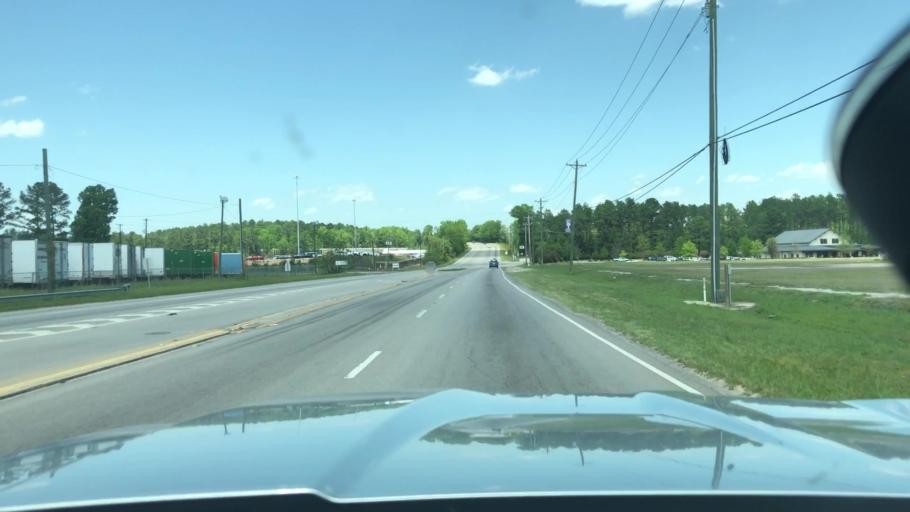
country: US
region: South Carolina
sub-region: Lexington County
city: Pineridge
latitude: 33.9029
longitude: -81.0648
